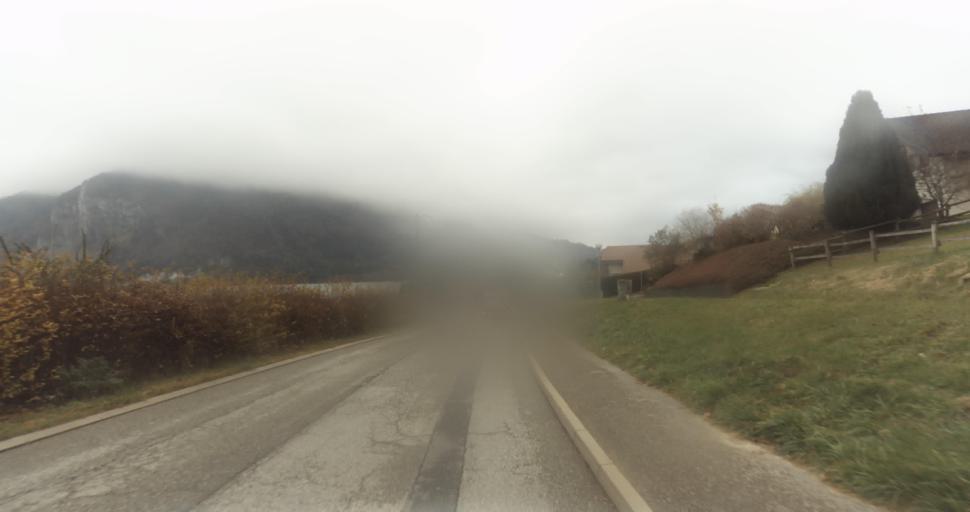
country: FR
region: Rhone-Alpes
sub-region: Departement de la Haute-Savoie
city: Thorens-Glieres
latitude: 45.9998
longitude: 6.2509
